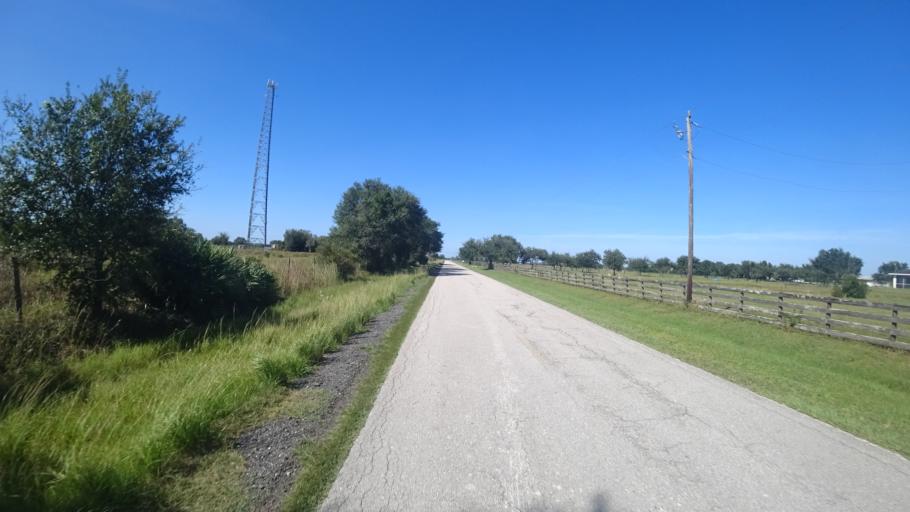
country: US
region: Florida
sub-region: Sarasota County
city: Warm Mineral Springs
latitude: 27.2738
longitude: -82.1794
